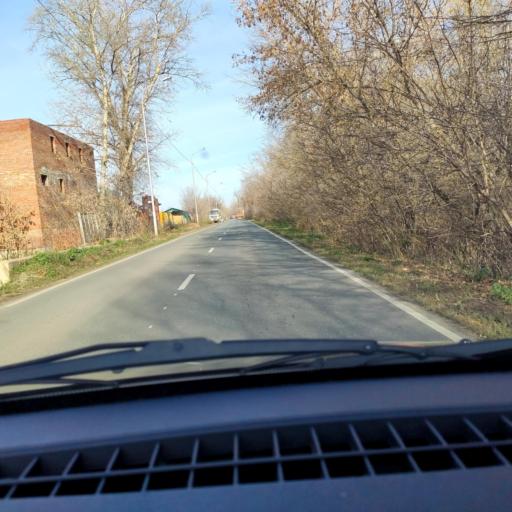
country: RU
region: Bashkortostan
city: Ufa
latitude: 54.6648
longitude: 55.9388
